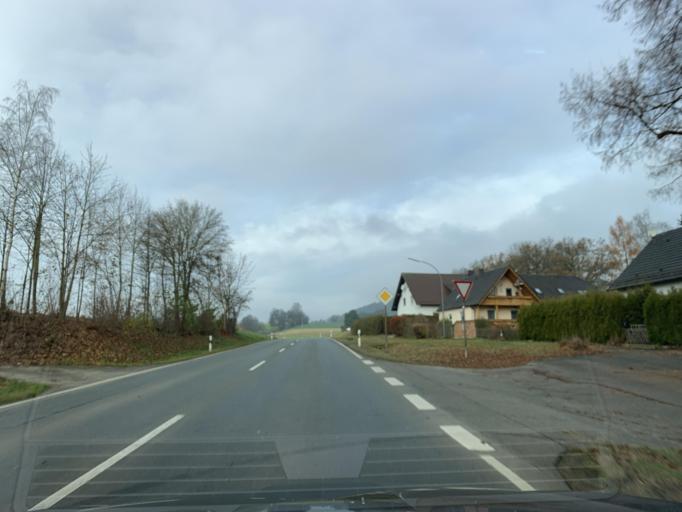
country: DE
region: Bavaria
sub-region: Upper Palatinate
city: Roetz
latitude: 49.3437
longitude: 12.5162
